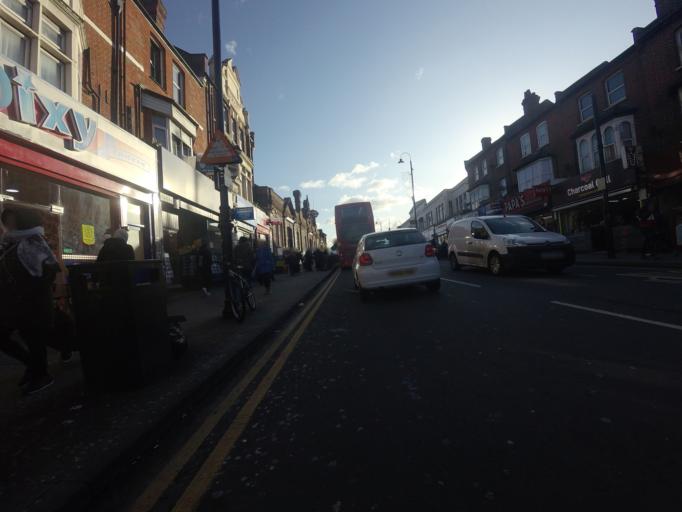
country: GB
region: England
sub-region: Greater London
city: East Ham
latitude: 51.5394
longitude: 0.0512
